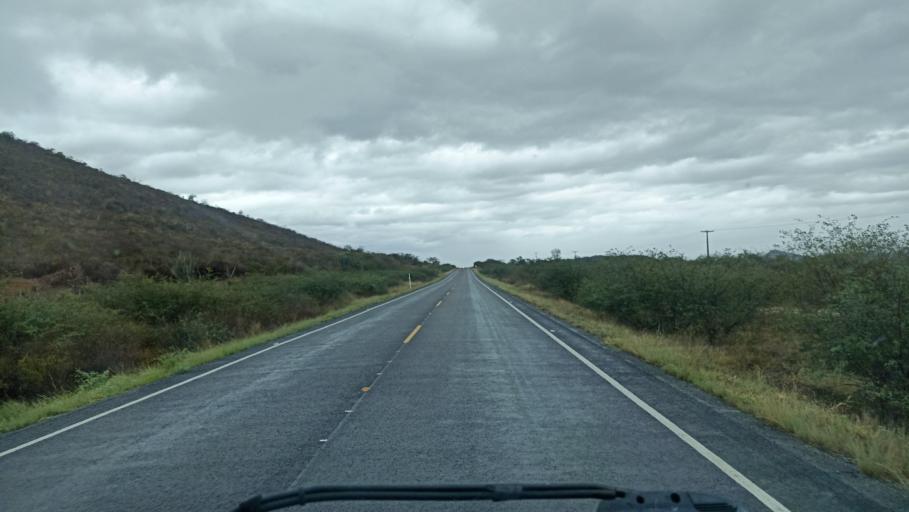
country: BR
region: Bahia
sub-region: Iacu
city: Iacu
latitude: -12.9579
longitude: -40.4716
